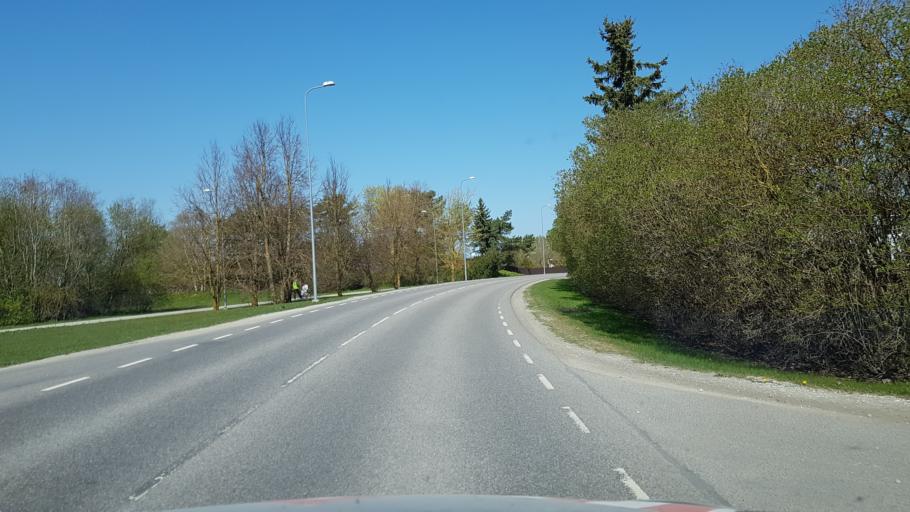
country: EE
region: Harju
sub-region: Joelaehtme vald
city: Loo
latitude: 59.4333
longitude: 24.9389
